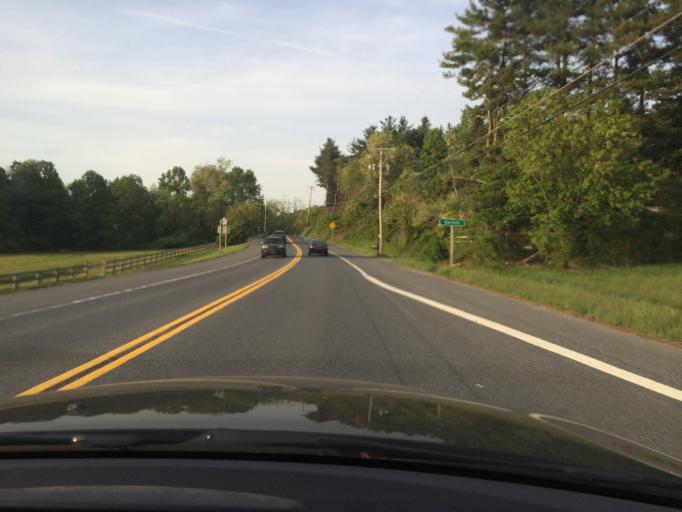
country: US
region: Maryland
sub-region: Carroll County
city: Sykesville
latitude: 39.4141
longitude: -77.0121
